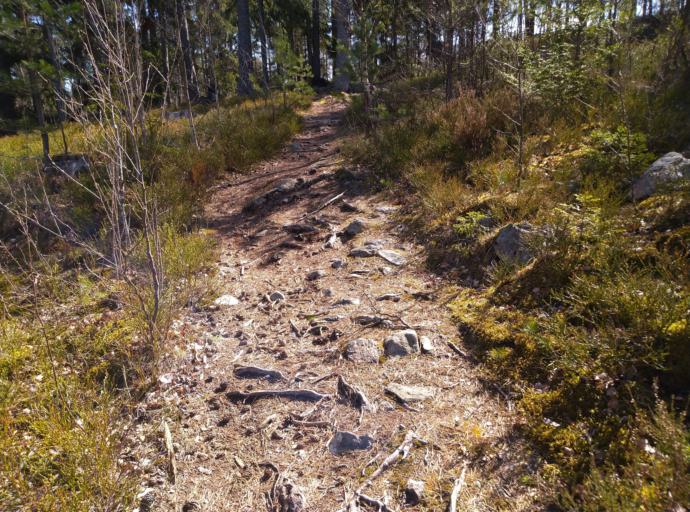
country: SE
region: Stockholm
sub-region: Nacka Kommun
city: Fisksatra
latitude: 59.2955
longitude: 18.2421
